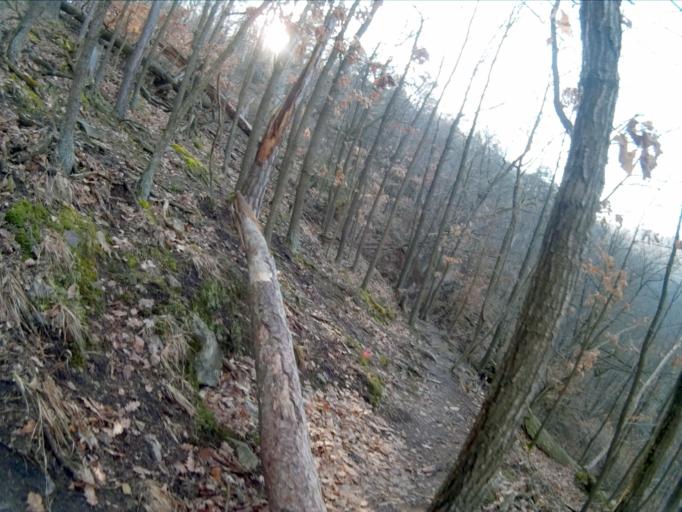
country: CZ
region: Vysocina
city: Namest' nad Oslavou
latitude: 49.1616
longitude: 16.1701
